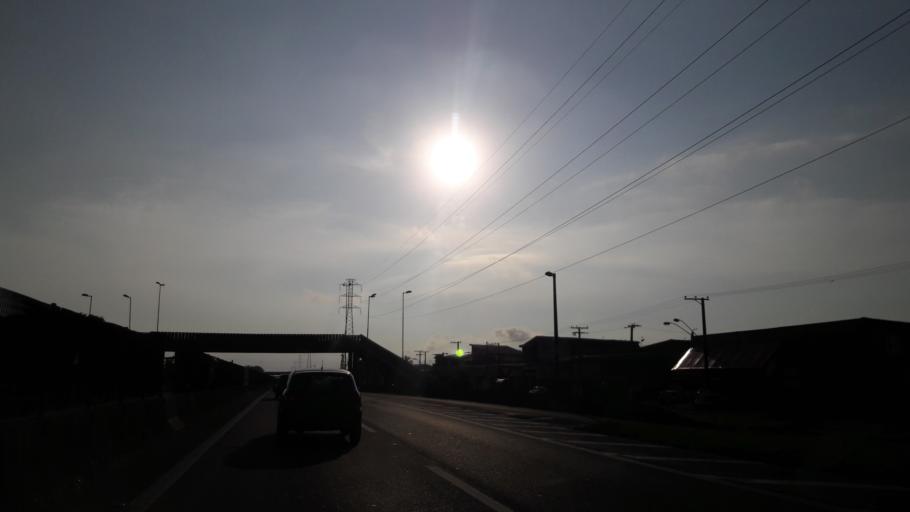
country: BR
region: Sao Paulo
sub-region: Mongagua
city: Mongagua
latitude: -24.1199
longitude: -46.6734
